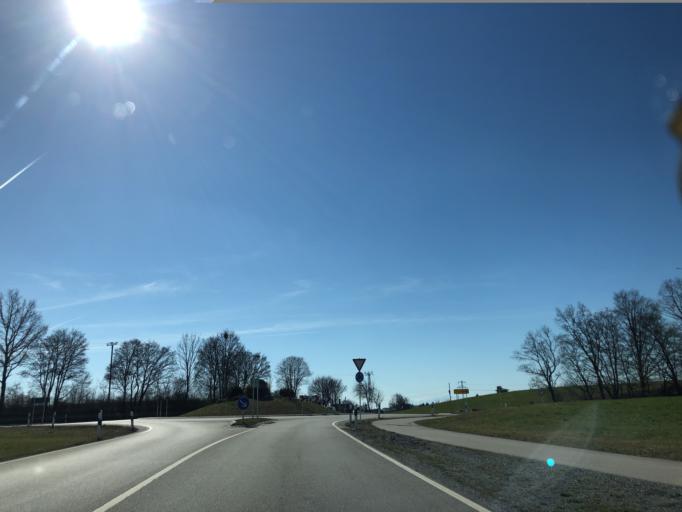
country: DE
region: Bavaria
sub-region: Upper Bavaria
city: Pfaffing
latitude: 48.0627
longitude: 12.1109
